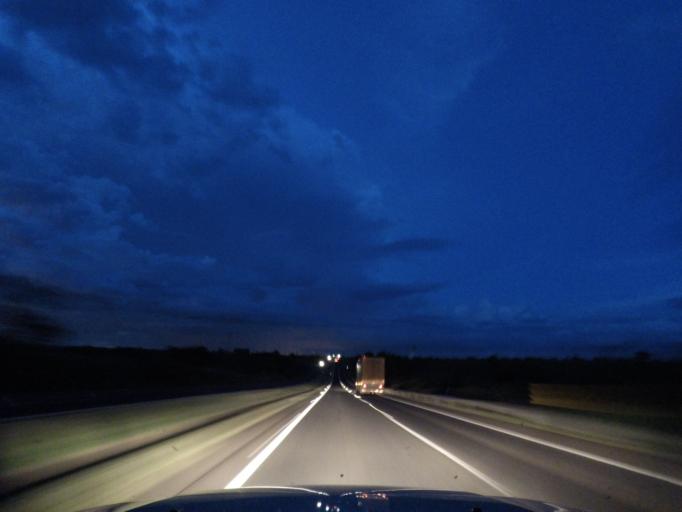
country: BR
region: Minas Gerais
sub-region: Uberlandia
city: Uberlandia
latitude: -19.2182
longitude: -48.1464
